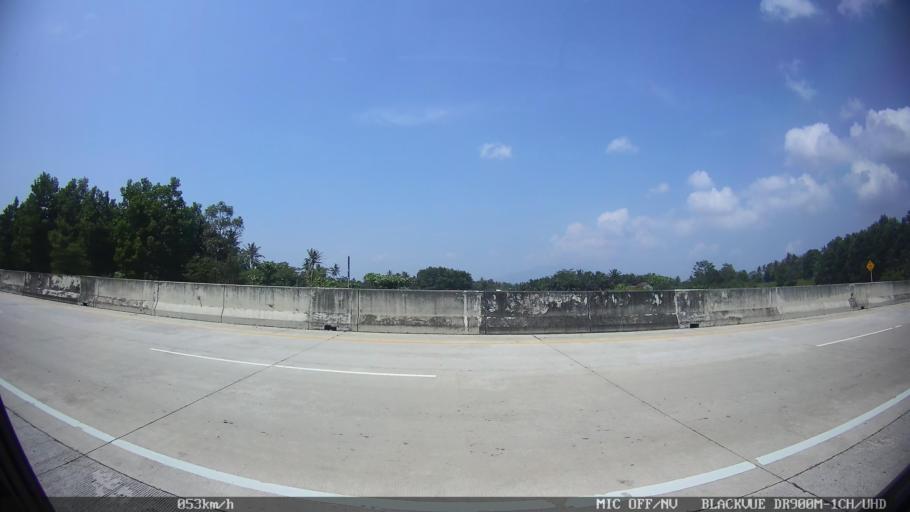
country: ID
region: Lampung
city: Kedaton
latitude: -5.3173
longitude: 105.2614
